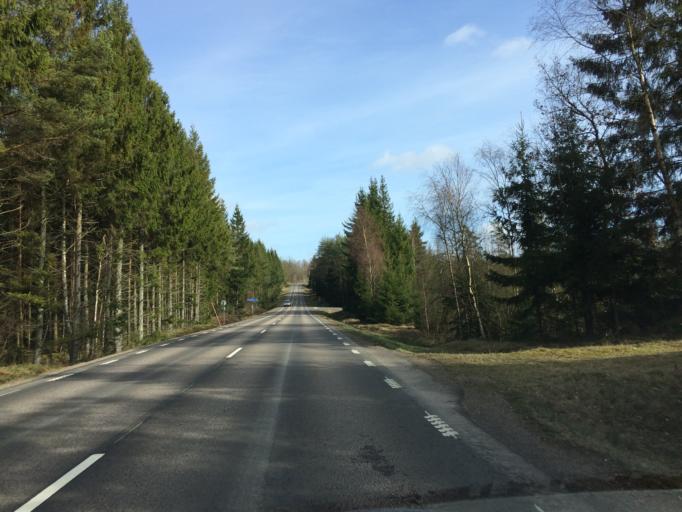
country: SE
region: Halland
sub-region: Hylte Kommun
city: Torup
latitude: 57.0240
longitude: 13.1266
